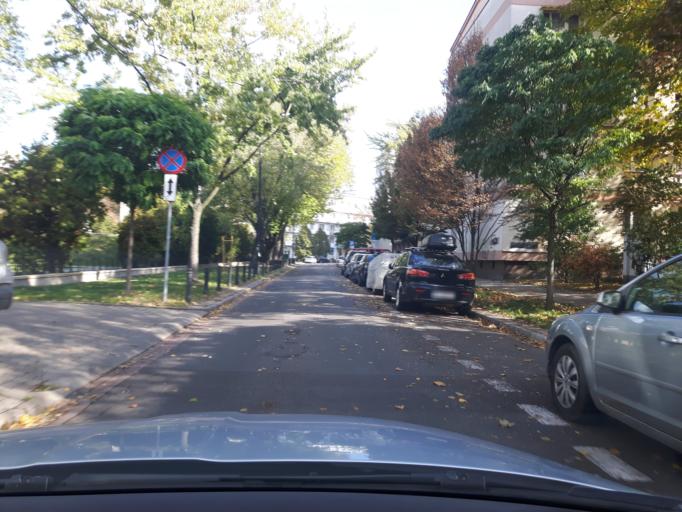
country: PL
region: Masovian Voivodeship
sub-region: Warszawa
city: Wola
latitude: 52.2512
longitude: 20.9919
